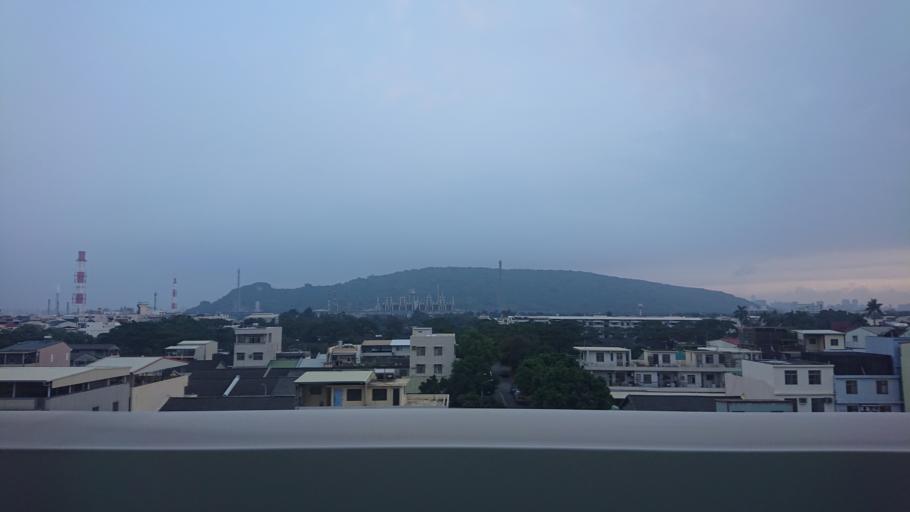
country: TW
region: Kaohsiung
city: Kaohsiung
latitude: 22.7180
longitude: 120.3058
